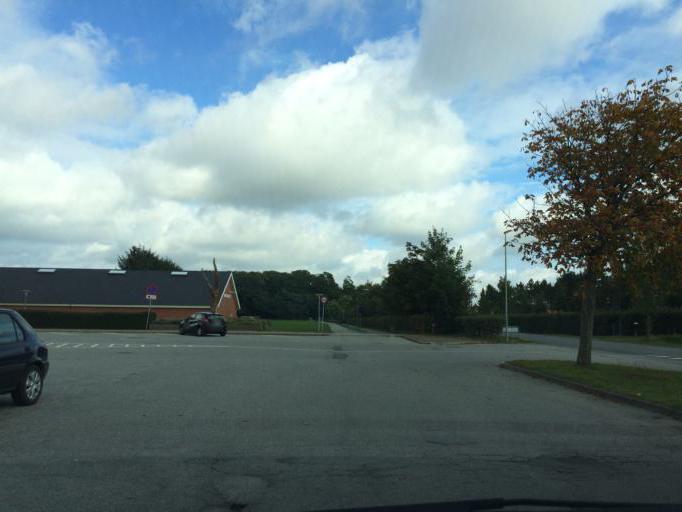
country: DK
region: North Denmark
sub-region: Bronderslev Kommune
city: Dronninglund
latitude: 57.1515
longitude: 10.2866
